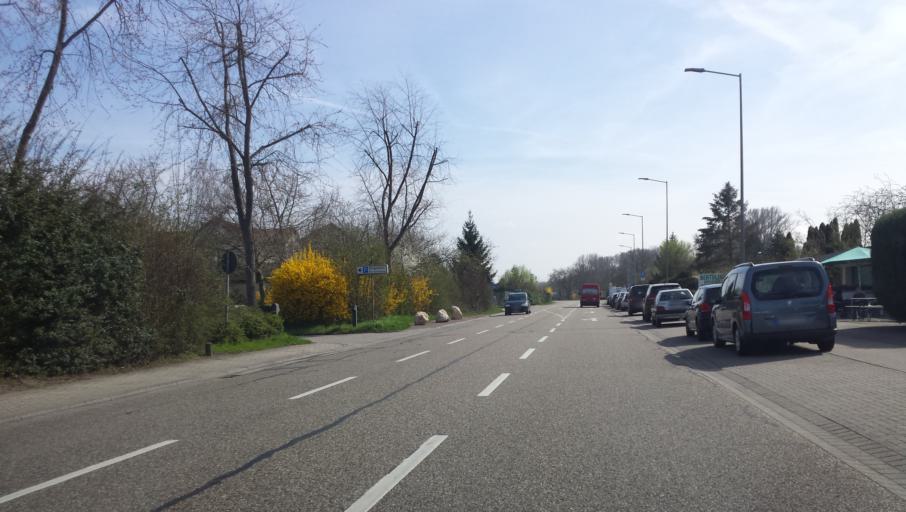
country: DE
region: Rheinland-Pfalz
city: Speyer
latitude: 49.3032
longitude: 8.4482
